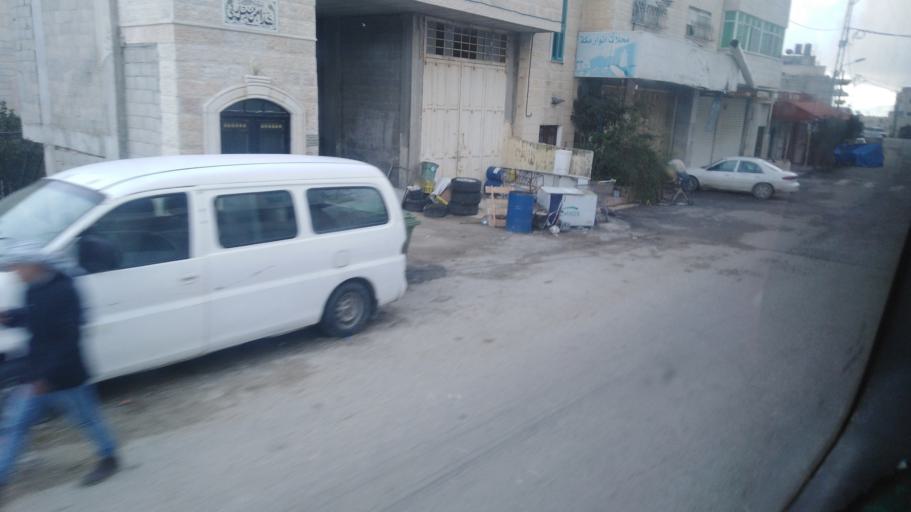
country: PS
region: West Bank
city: Hebron
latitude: 31.5270
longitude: 35.0776
